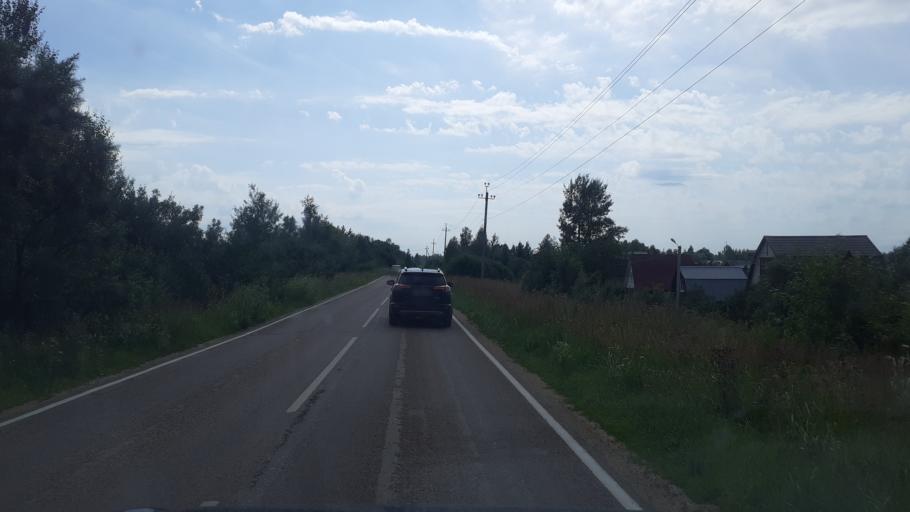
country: RU
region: Moskovskaya
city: Chupryakovo
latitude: 55.5644
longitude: 36.5687
